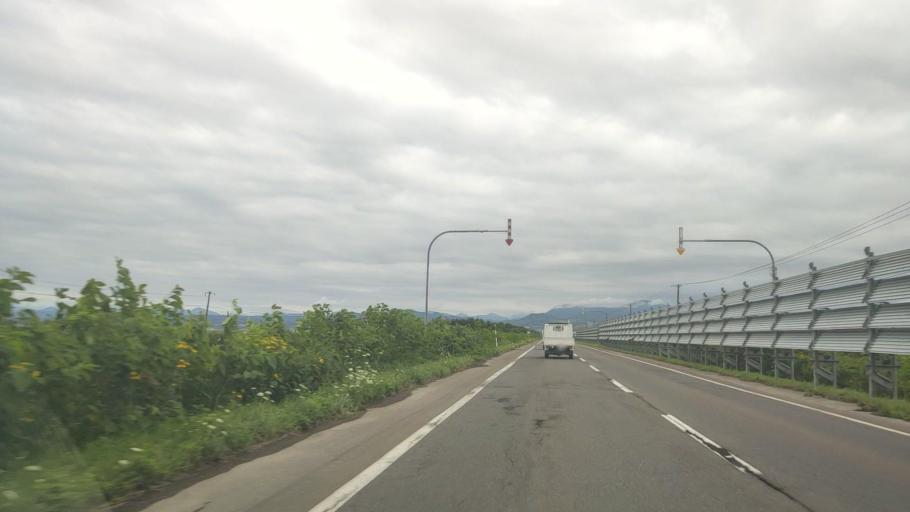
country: JP
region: Hokkaido
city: Nanae
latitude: 42.3007
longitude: 140.2720
